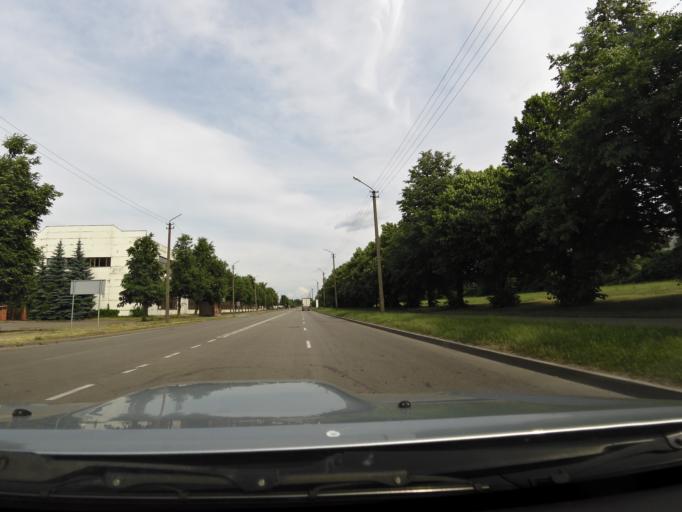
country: LT
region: Marijampoles apskritis
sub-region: Marijampole Municipality
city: Marijampole
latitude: 54.5750
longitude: 23.3724
